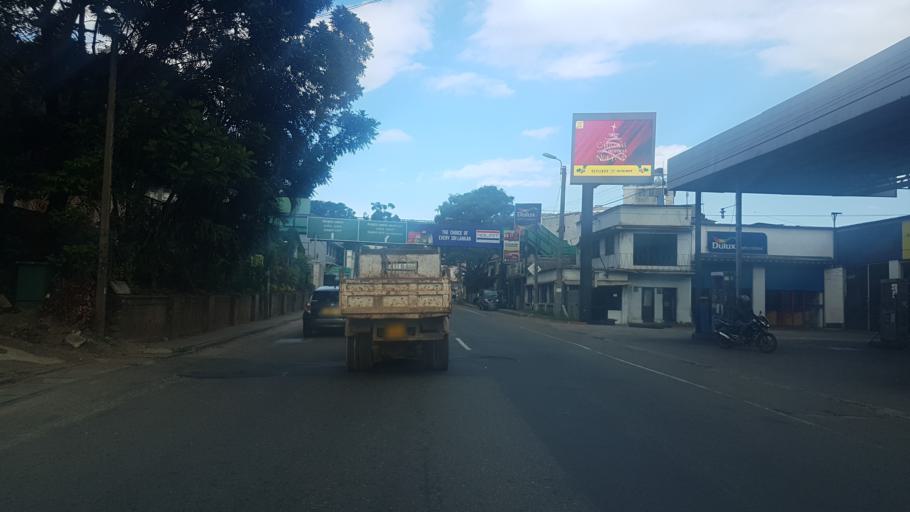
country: LK
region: Central
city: Kandy
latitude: 7.2860
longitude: 80.6264
